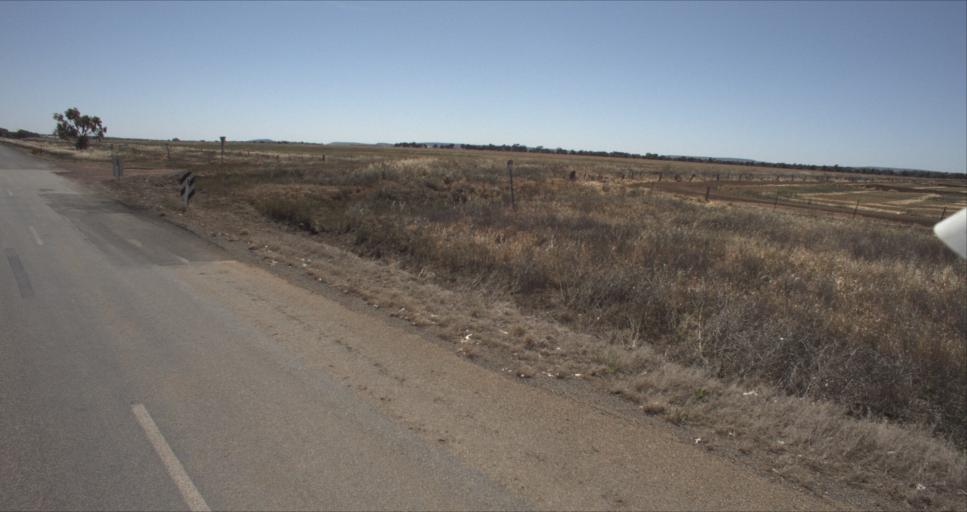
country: AU
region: New South Wales
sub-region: Leeton
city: Leeton
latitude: -34.4935
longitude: 146.2883
